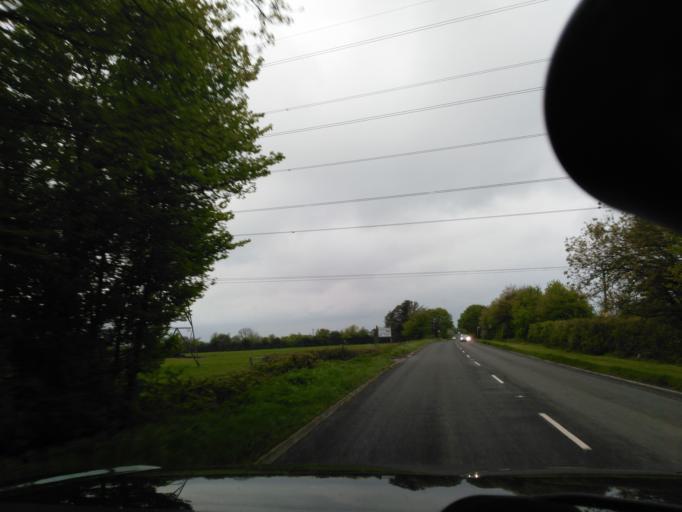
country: GB
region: England
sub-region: Wiltshire
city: Melksham
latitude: 51.3380
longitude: -2.1562
